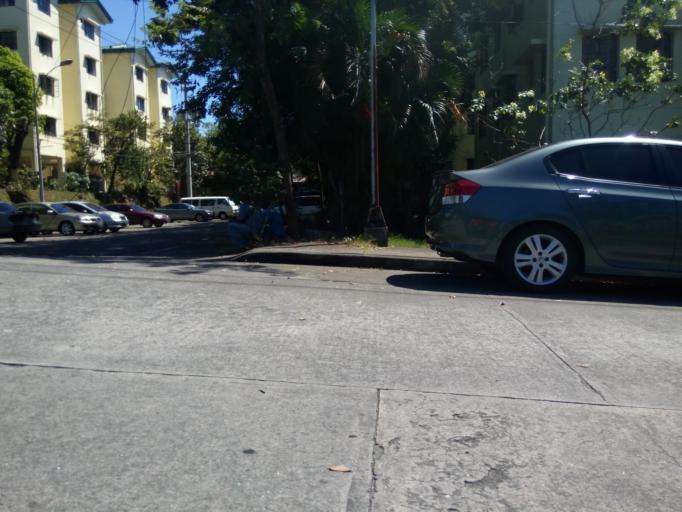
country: PH
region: Metro Manila
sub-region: Quezon City
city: Quezon City
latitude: 14.6437
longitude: 121.0696
